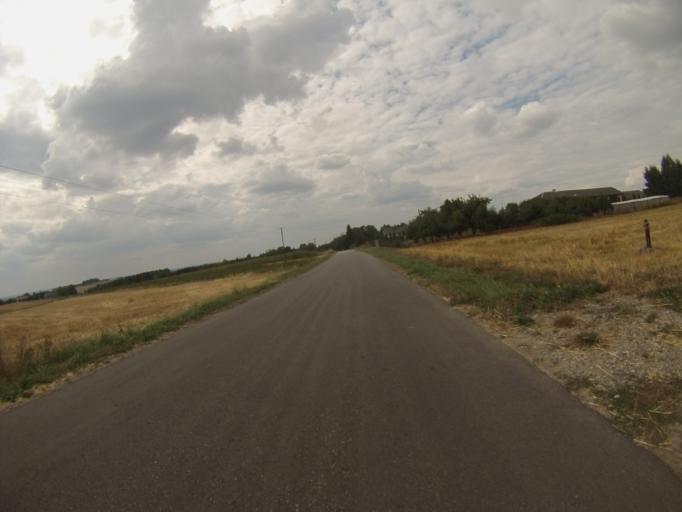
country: PL
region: Swietokrzyskie
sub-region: Powiat kielecki
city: Lagow
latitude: 50.7142
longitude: 21.1113
